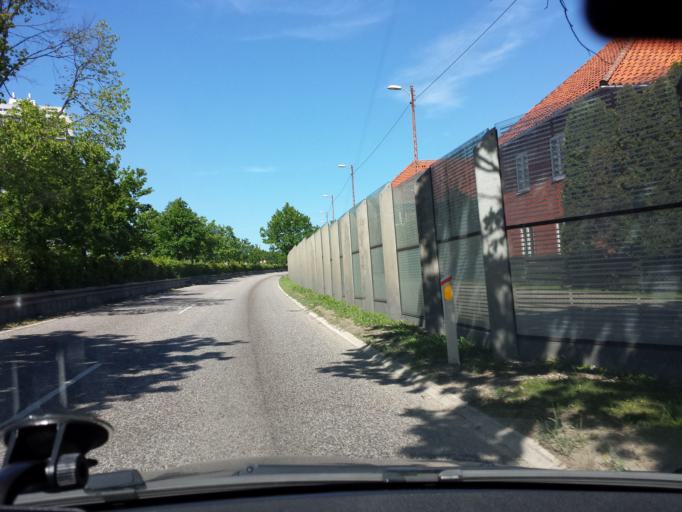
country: DK
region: Capital Region
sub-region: Herlev Kommune
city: Herlev
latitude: 55.7281
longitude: 12.4433
